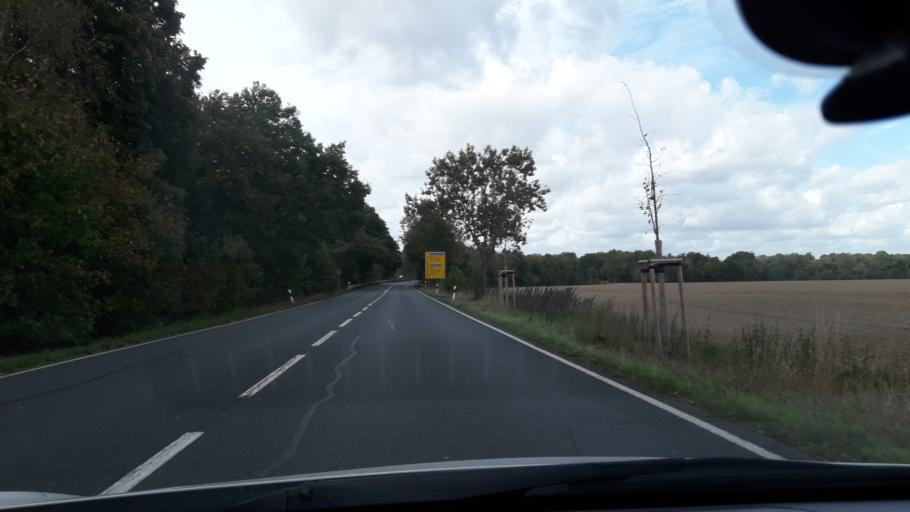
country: DE
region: Lower Saxony
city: Alt Wallmoden
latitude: 52.0200
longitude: 10.3590
